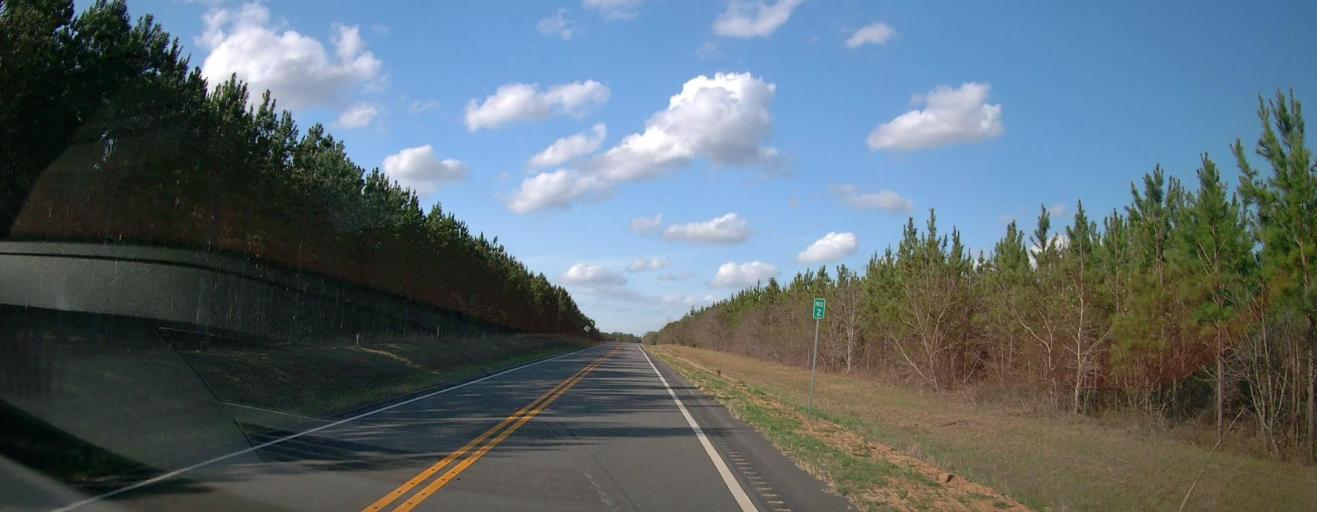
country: US
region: Georgia
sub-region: Wheeler County
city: Alamo
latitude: 32.0805
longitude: -82.8111
